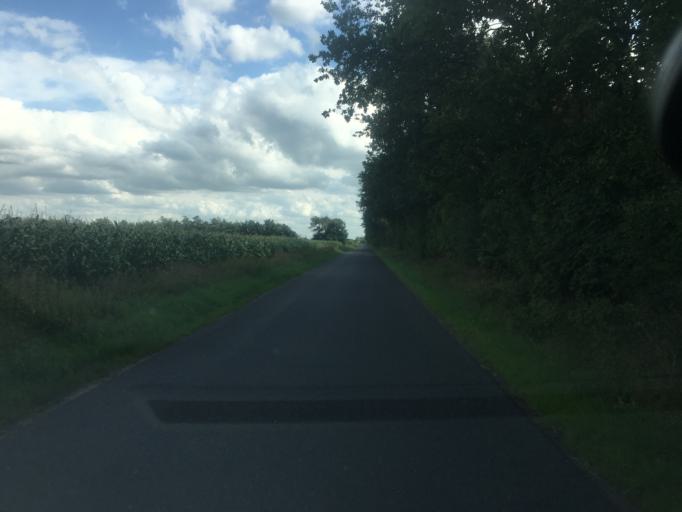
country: DK
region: South Denmark
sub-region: Tonder Kommune
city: Logumkloster
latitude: 55.0102
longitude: 9.0042
